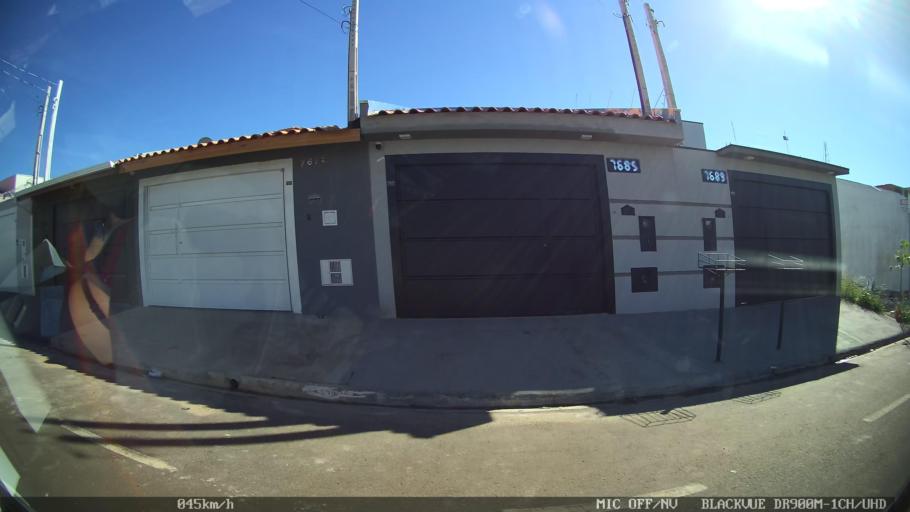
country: BR
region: Sao Paulo
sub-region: Franca
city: Franca
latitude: -20.5674
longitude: -47.3457
